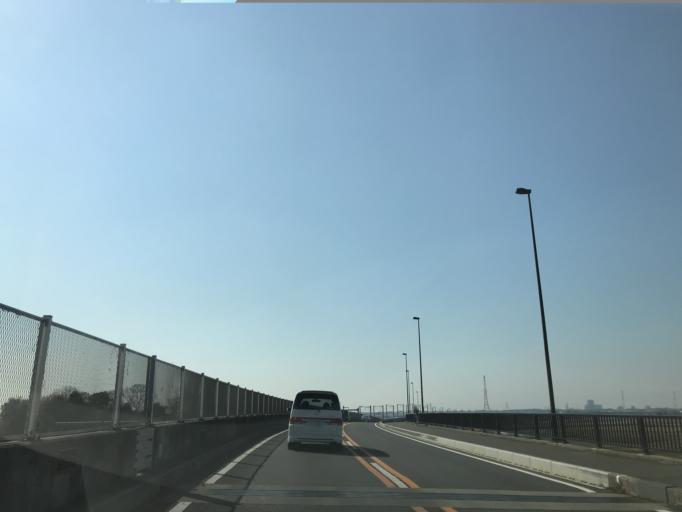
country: JP
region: Ibaraki
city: Mitsukaido
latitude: 35.9910
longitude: 140.0360
